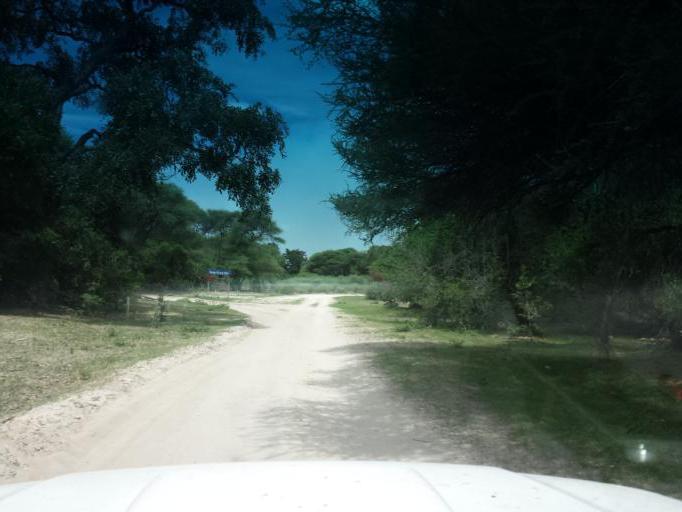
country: BW
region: North West
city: Shakawe
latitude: -18.7474
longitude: 22.1942
